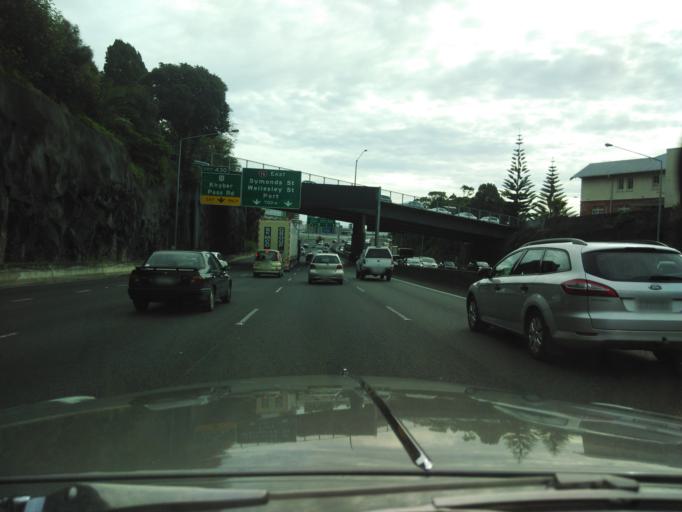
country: NZ
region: Auckland
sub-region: Auckland
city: Auckland
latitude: -36.8691
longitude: 174.7703
